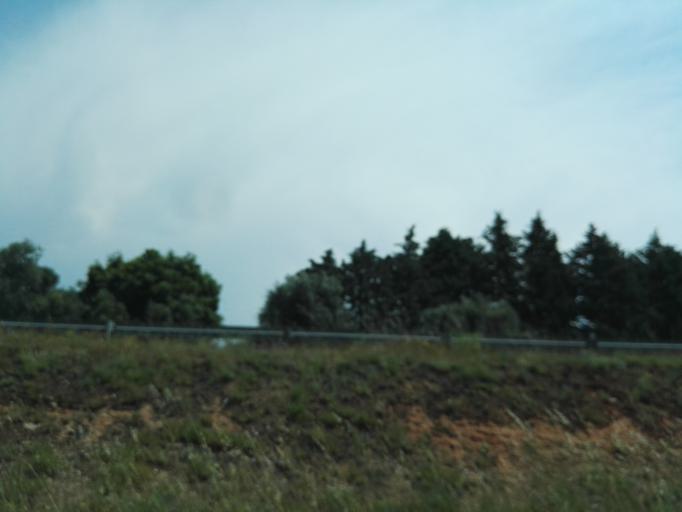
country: PT
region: Santarem
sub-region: Entroncamento
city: Entroncamento
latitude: 39.4632
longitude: -8.4562
